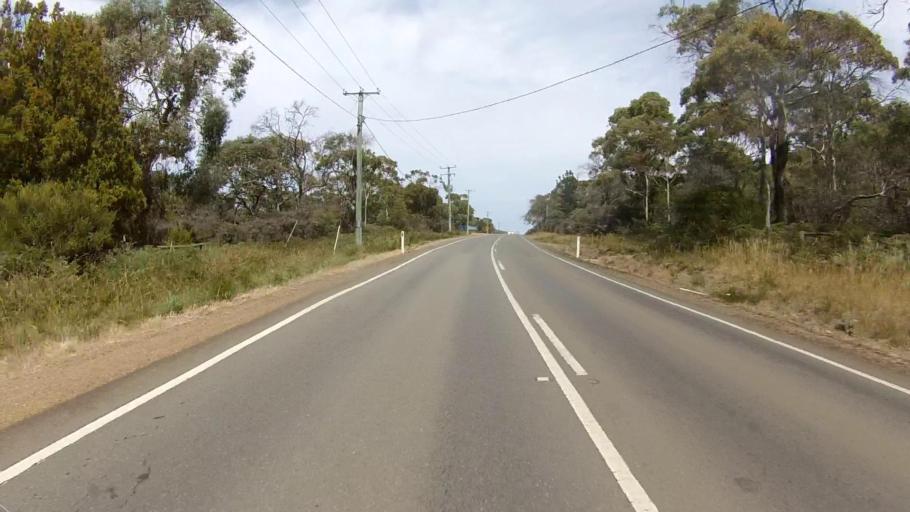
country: AU
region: Tasmania
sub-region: Clarence
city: Sandford
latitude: -43.0196
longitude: 147.4884
